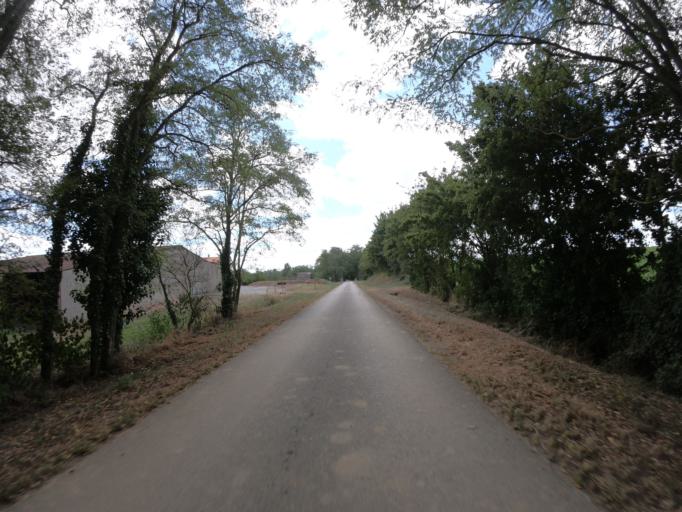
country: FR
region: Midi-Pyrenees
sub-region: Departement de l'Ariege
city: La Tour-du-Crieu
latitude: 43.1026
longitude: 1.7275
